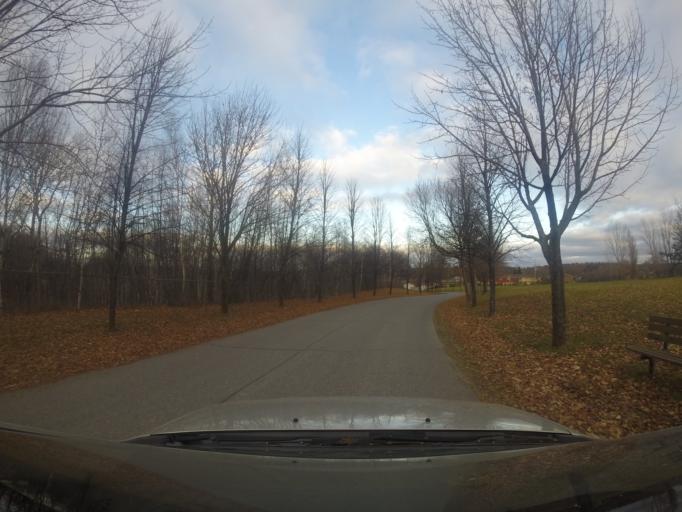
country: CA
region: Ontario
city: Greater Sudbury
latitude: 46.4993
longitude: -80.9383
